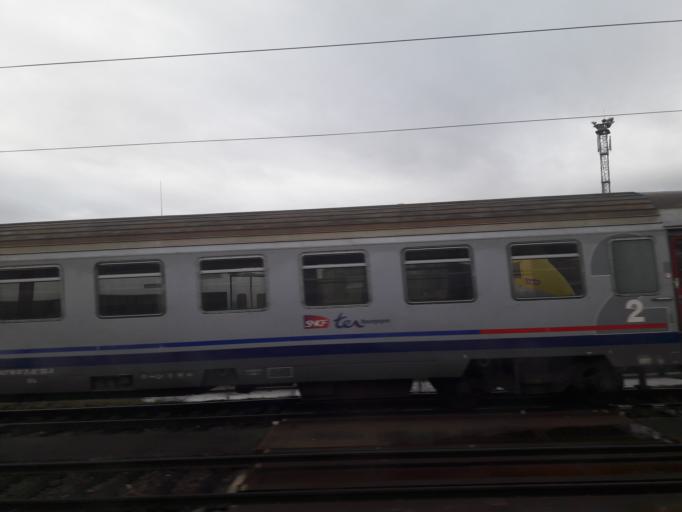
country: FR
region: Franche-Comte
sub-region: Territoire de Belfort
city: Belfort
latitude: 47.6272
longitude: 6.8568
